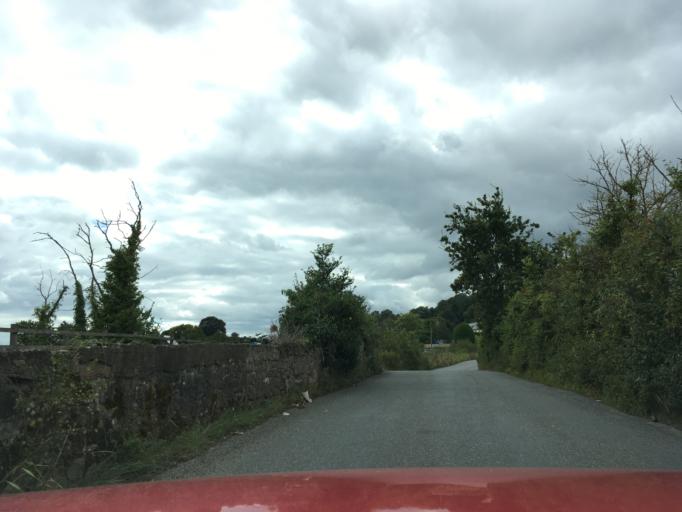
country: GB
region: England
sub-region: Devon
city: Starcross
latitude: 50.6111
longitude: -3.4454
